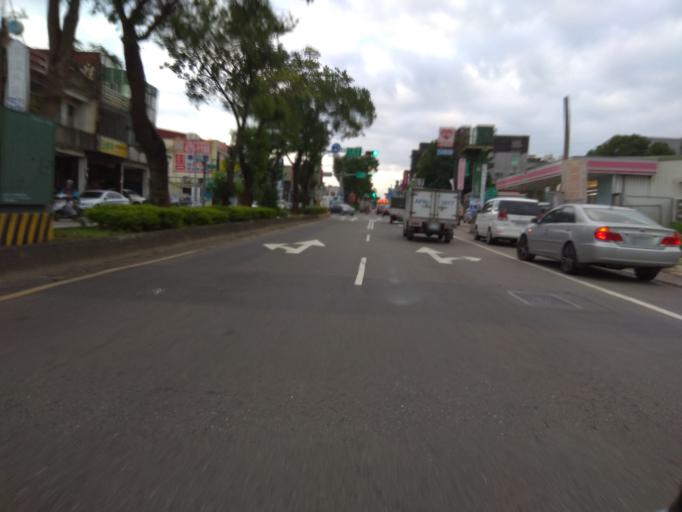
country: TW
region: Taiwan
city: Daxi
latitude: 24.8889
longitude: 121.2126
